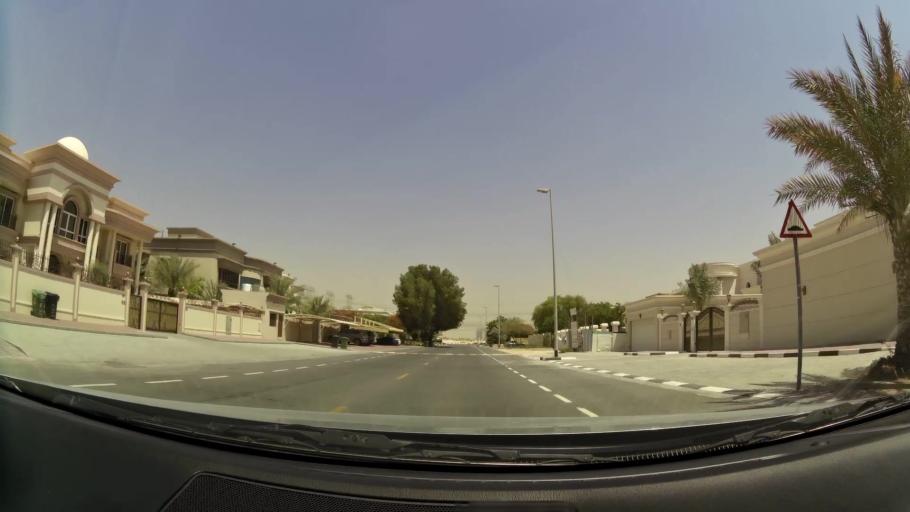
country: AE
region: Dubai
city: Dubai
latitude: 25.0932
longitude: 55.2168
